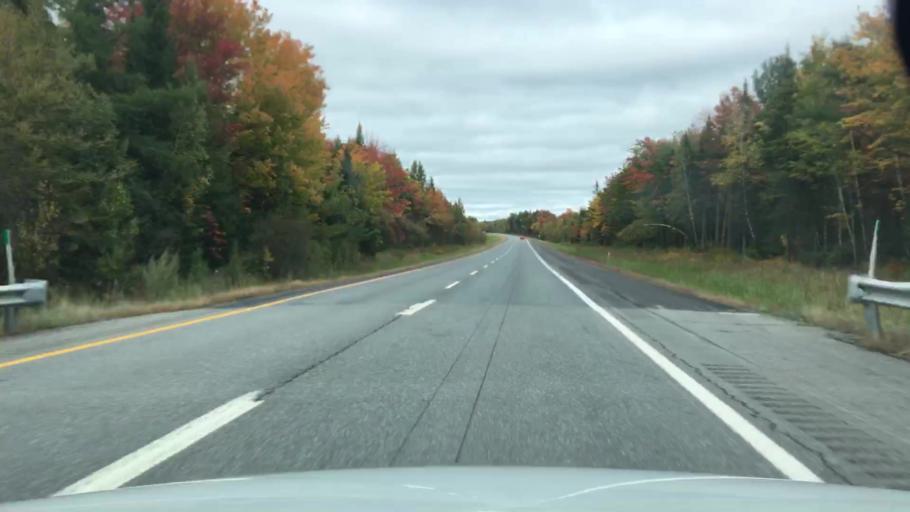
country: US
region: Maine
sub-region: Waldo County
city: Burnham
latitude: 44.7051
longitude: -69.4553
